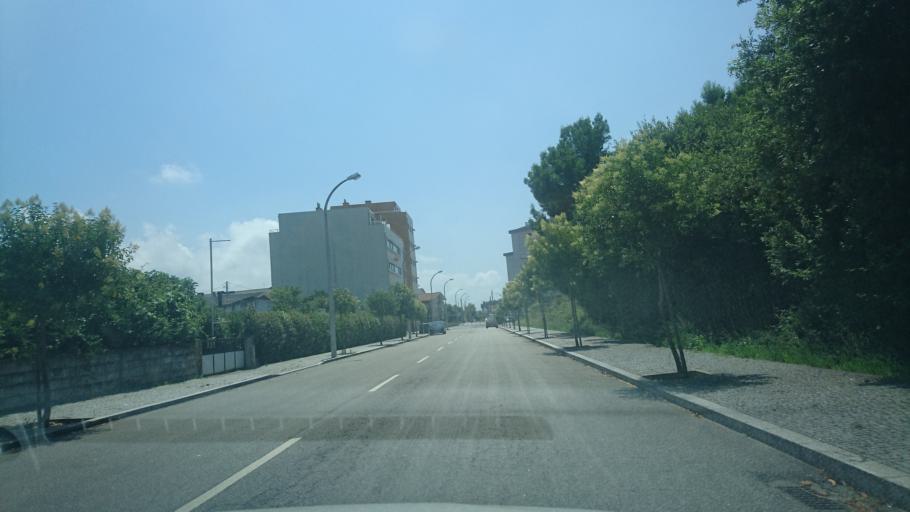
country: PT
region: Aveiro
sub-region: Ovar
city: Esmoriz
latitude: 40.9564
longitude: -8.6308
